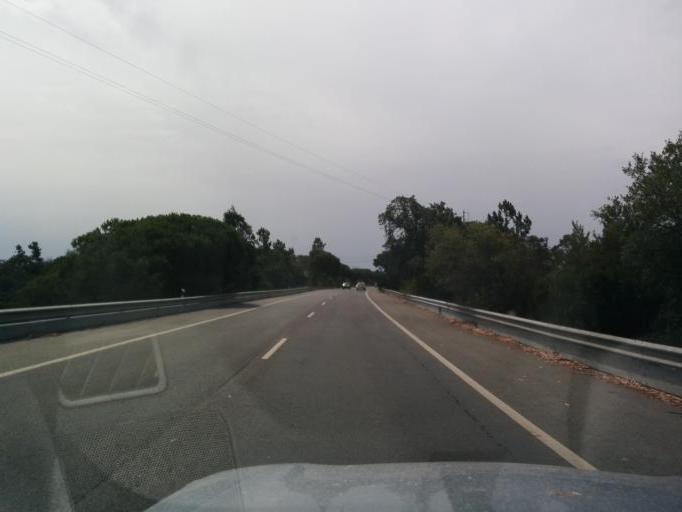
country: PT
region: Beja
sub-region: Odemira
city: Vila Nova de Milfontes
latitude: 37.7220
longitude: -8.7675
